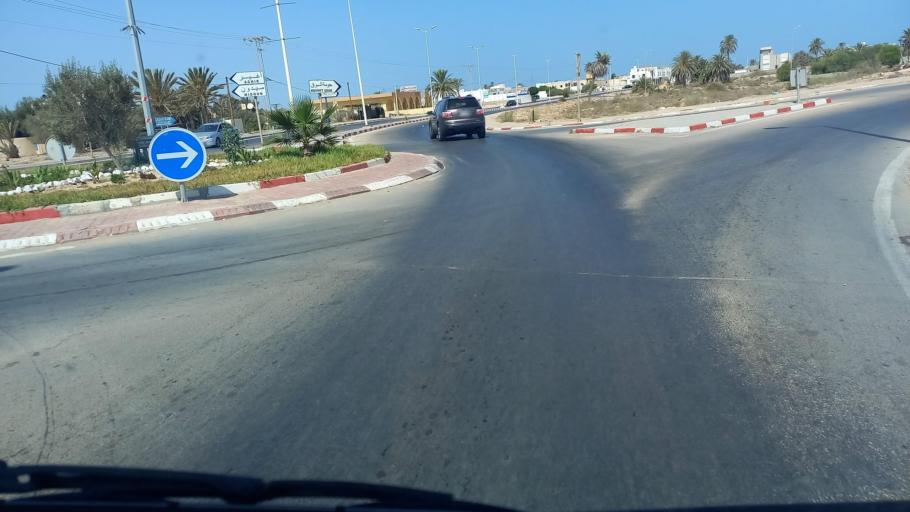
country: TN
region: Madanin
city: Midoun
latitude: 33.8619
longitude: 10.9656
